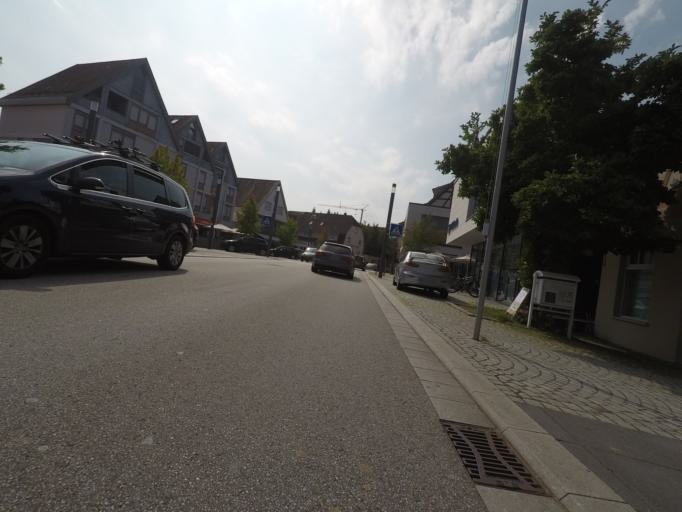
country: DE
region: Baden-Wuerttemberg
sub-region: Regierungsbezirk Stuttgart
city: Winterbach
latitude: 48.7992
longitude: 9.4791
